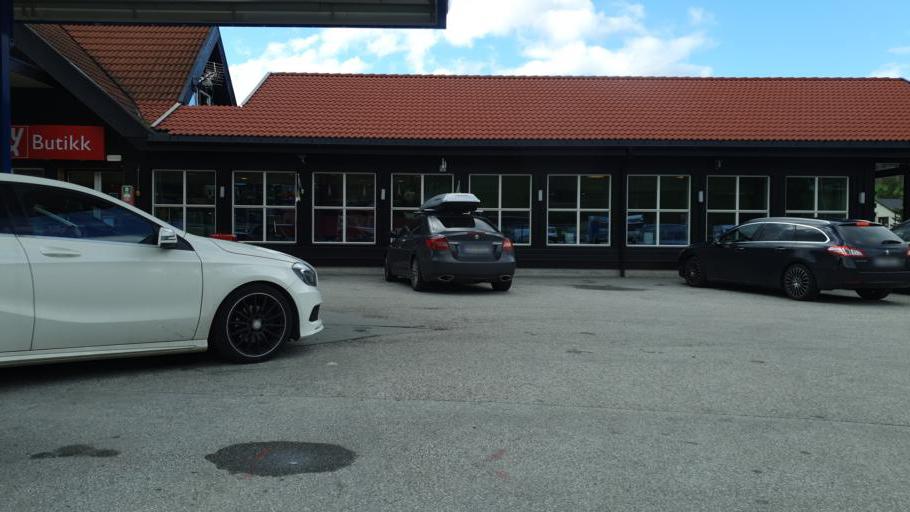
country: NO
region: Oppland
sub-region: Vaga
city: Vagamo
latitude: 61.8696
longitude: 9.1034
